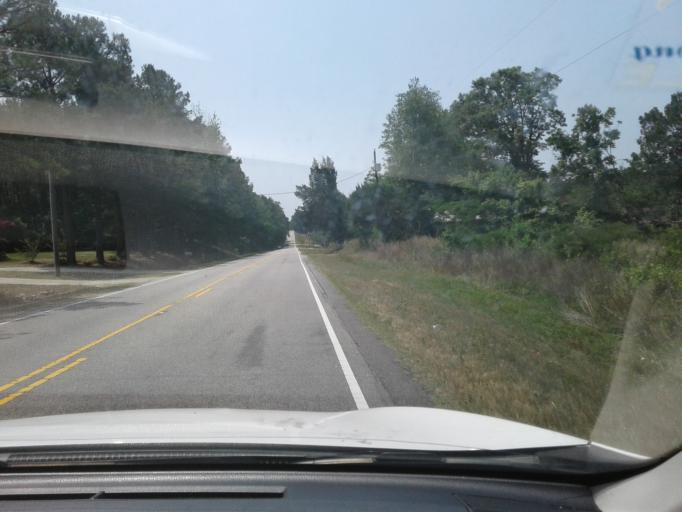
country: US
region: North Carolina
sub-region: Harnett County
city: Coats
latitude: 35.4360
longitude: -78.6803
